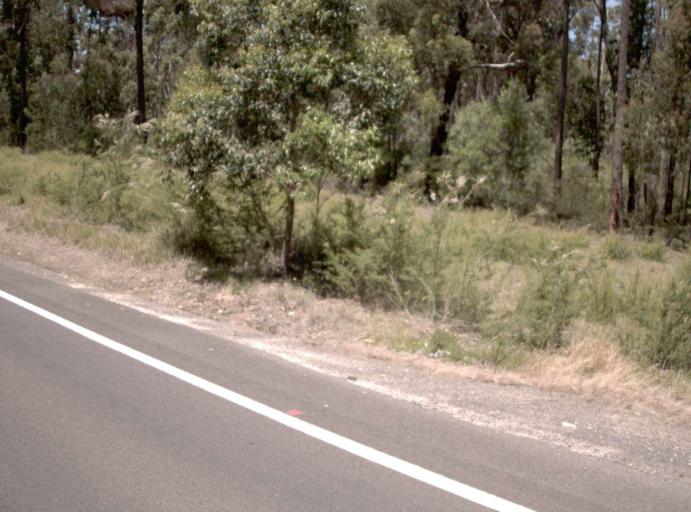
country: AU
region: Victoria
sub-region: East Gippsland
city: Lakes Entrance
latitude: -37.7452
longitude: 148.3898
